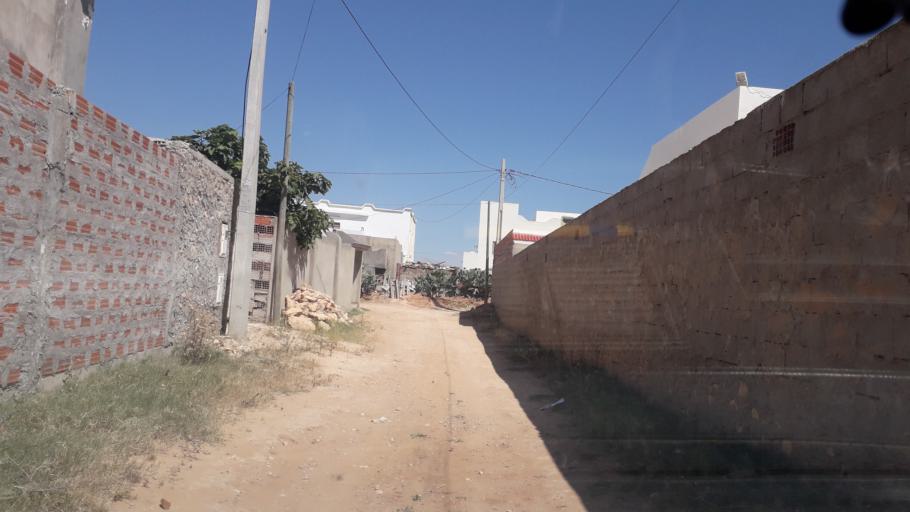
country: TN
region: Safaqis
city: Al Qarmadah
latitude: 34.8310
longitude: 10.7673
